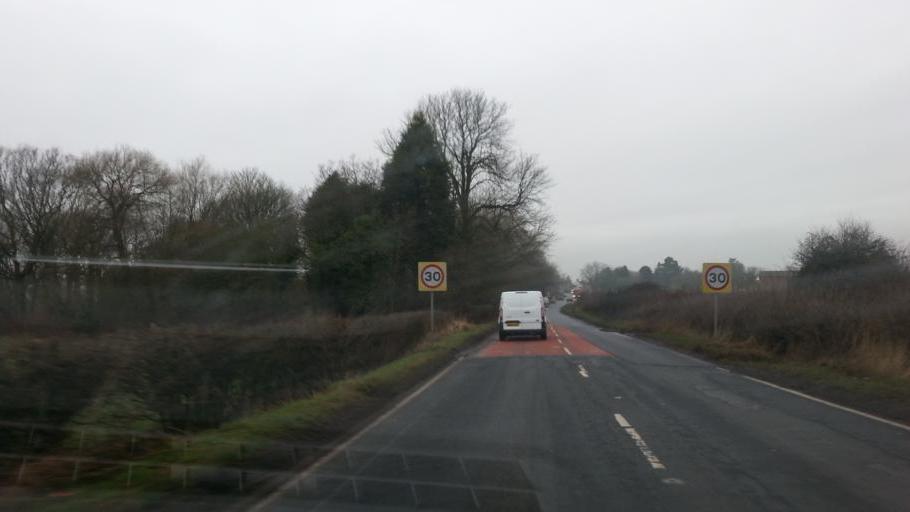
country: GB
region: England
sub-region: City and Borough of Wakefield
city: Low Ackworth
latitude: 53.6575
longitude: -1.3011
